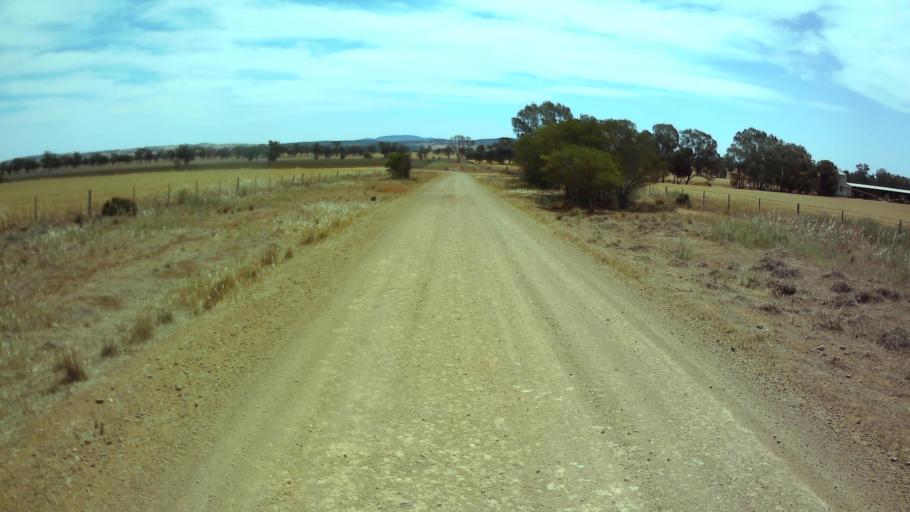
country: AU
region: New South Wales
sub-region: Weddin
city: Grenfell
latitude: -33.7495
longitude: 148.1476
